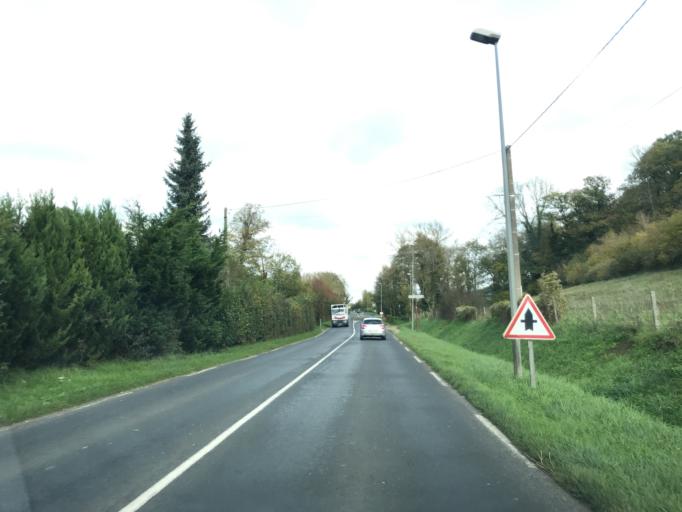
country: FR
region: Haute-Normandie
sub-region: Departement de l'Eure
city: Les Andelys
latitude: 49.2605
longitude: 1.4206
